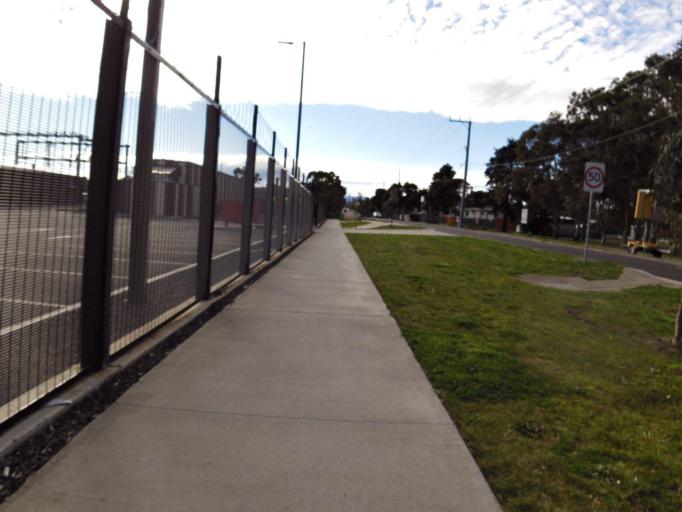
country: AU
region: Victoria
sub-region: Whittlesea
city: Mernda
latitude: -37.5968
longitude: 145.1023
